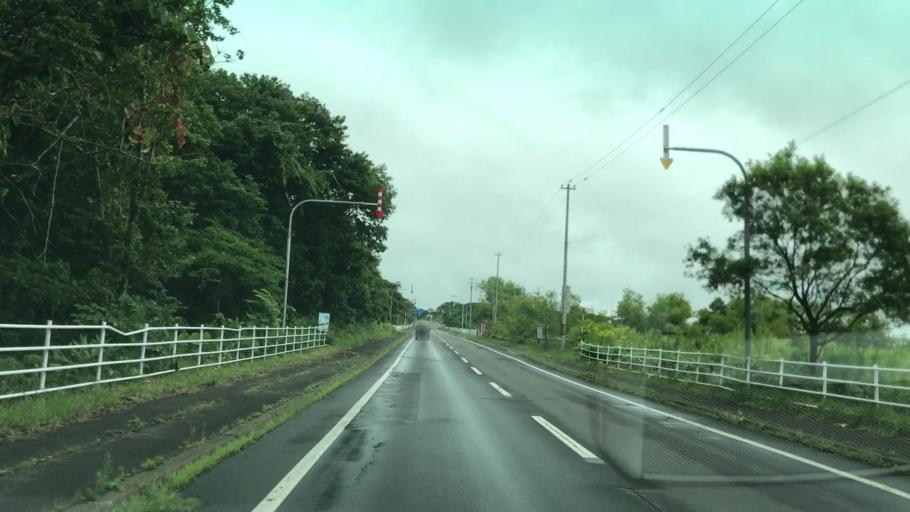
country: JP
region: Hokkaido
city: Muroran
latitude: 42.3903
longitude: 140.9932
